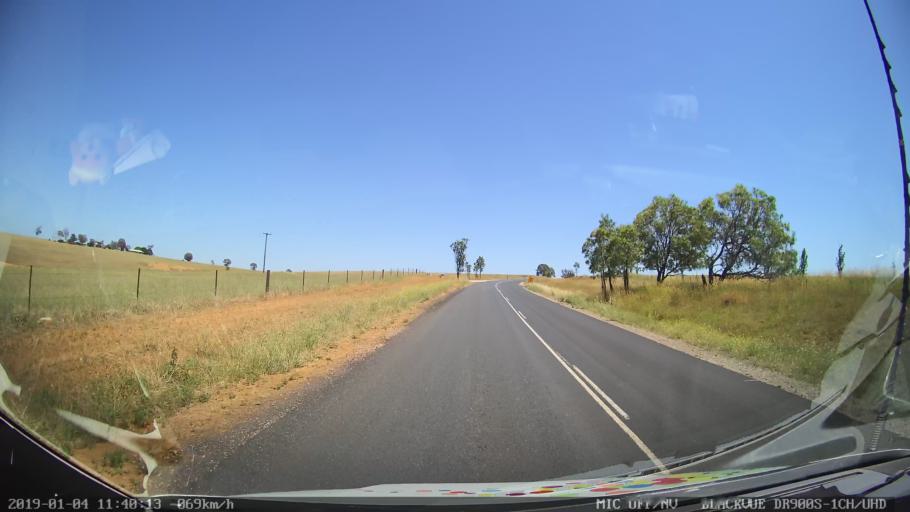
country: AU
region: New South Wales
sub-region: Cabonne
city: Molong
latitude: -33.0068
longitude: 148.7886
